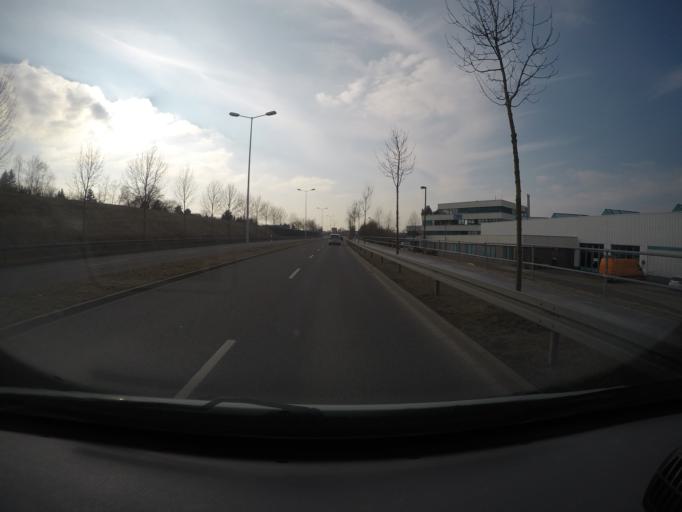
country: DE
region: Saxony
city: Hilbersdorf
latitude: 50.8192
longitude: 12.9722
